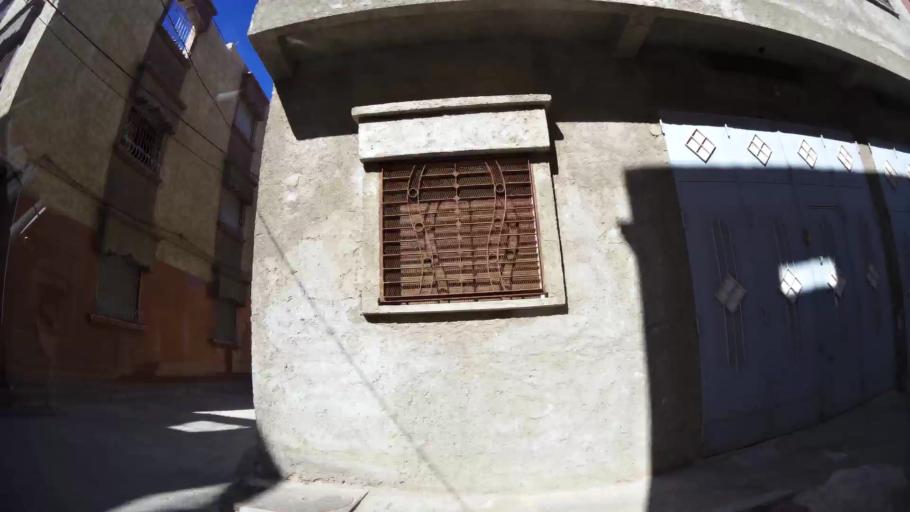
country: MA
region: Oriental
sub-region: Oujda-Angad
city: Oujda
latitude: 34.6565
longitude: -1.9511
